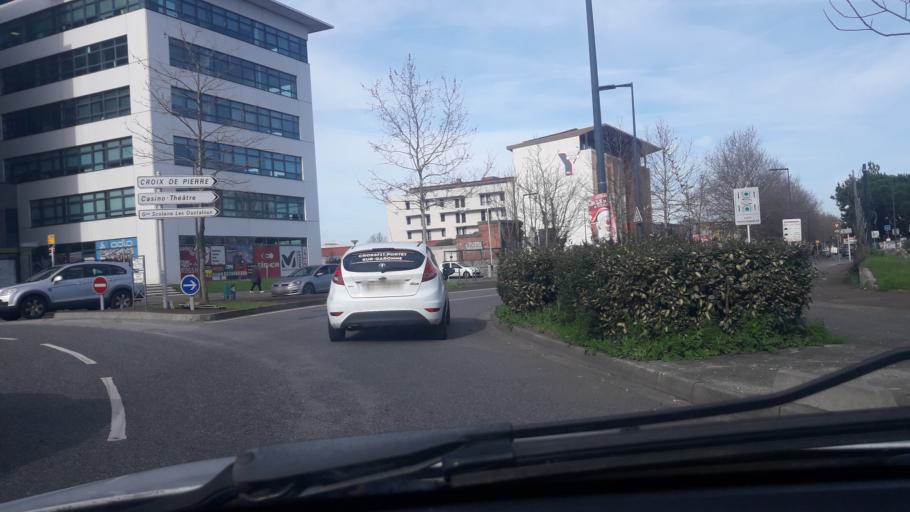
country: FR
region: Midi-Pyrenees
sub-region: Departement de la Haute-Garonne
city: Toulouse
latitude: 43.5701
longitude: 1.4247
